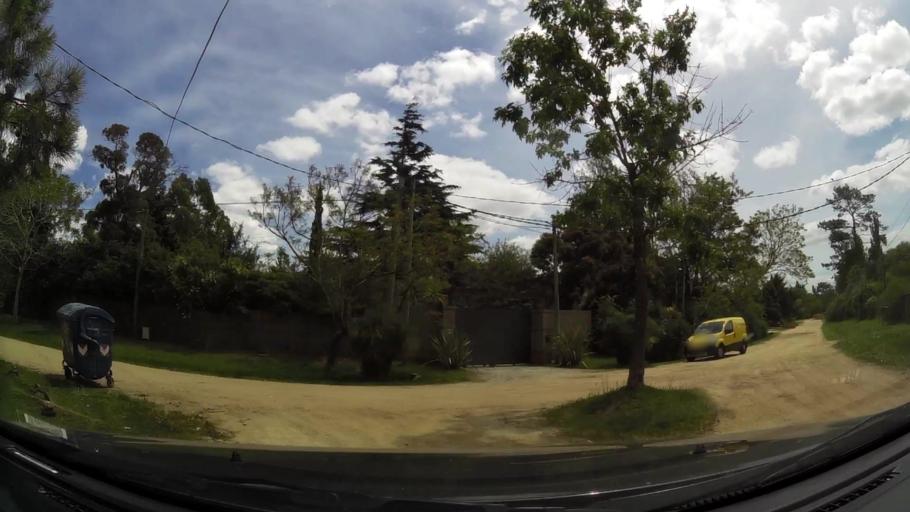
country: UY
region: Canelones
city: Pando
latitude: -34.8010
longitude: -55.8977
